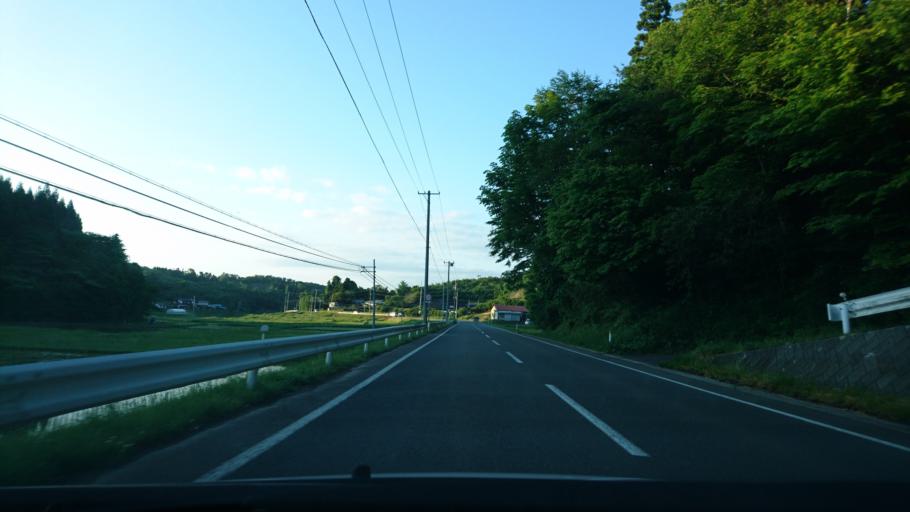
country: JP
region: Iwate
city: Ichinoseki
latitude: 38.8864
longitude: 141.1569
